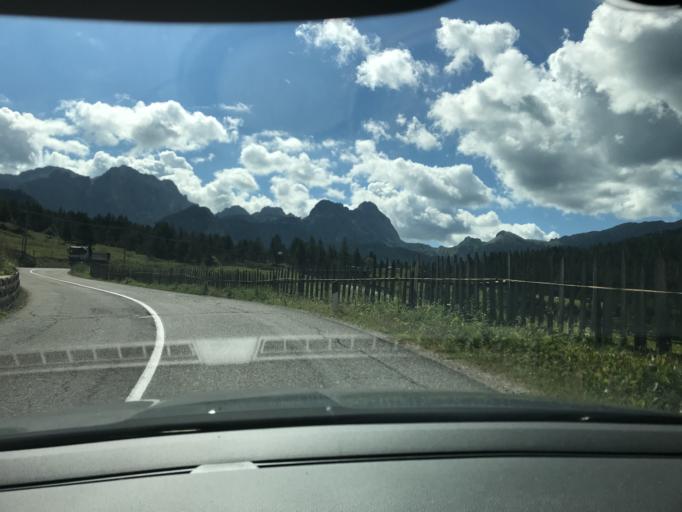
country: IT
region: Trentino-Alto Adige
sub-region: Bolzano
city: Badia
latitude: 46.5659
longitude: 11.9424
